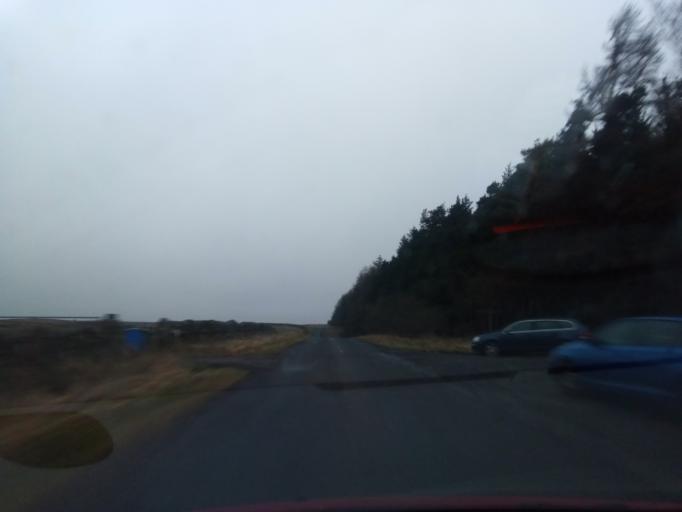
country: GB
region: England
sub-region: Northumberland
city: Otterburn
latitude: 55.2092
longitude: -2.0452
